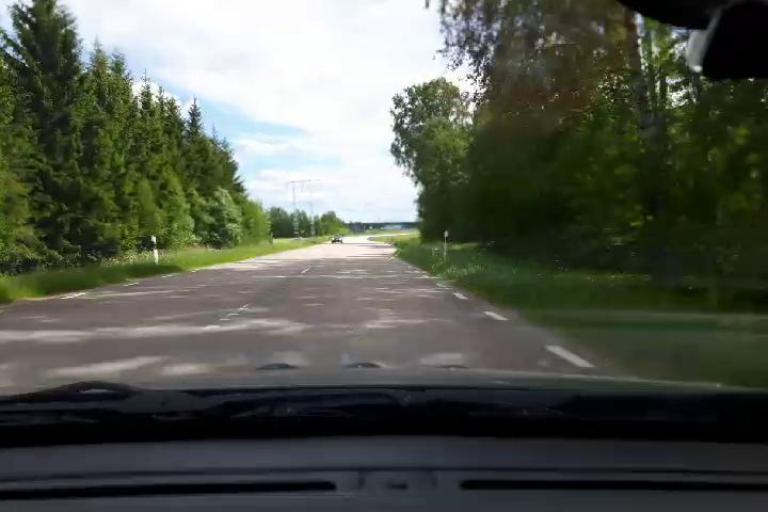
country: SE
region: Uppsala
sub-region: Tierps Kommun
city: Tierp
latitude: 60.3529
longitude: 17.4660
